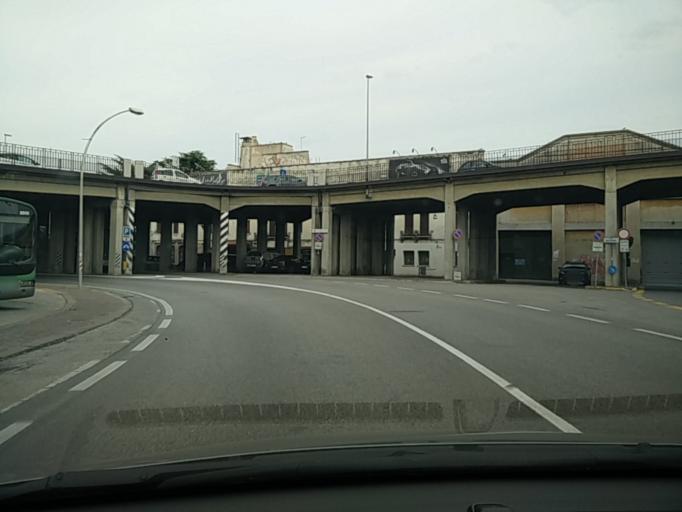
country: IT
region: Veneto
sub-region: Provincia di Treviso
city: Treviso
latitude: 45.6603
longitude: 12.2469
